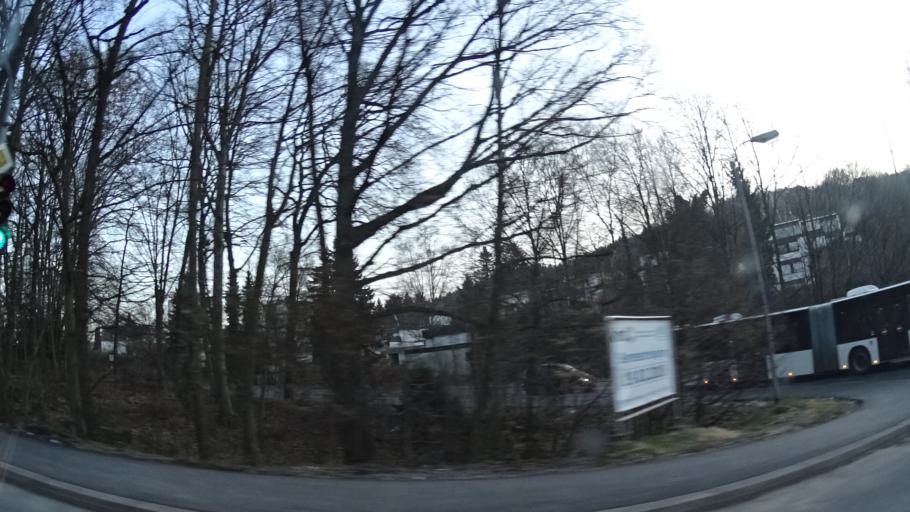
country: DE
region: Saarland
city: Sulzbach
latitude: 49.2652
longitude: 7.0493
